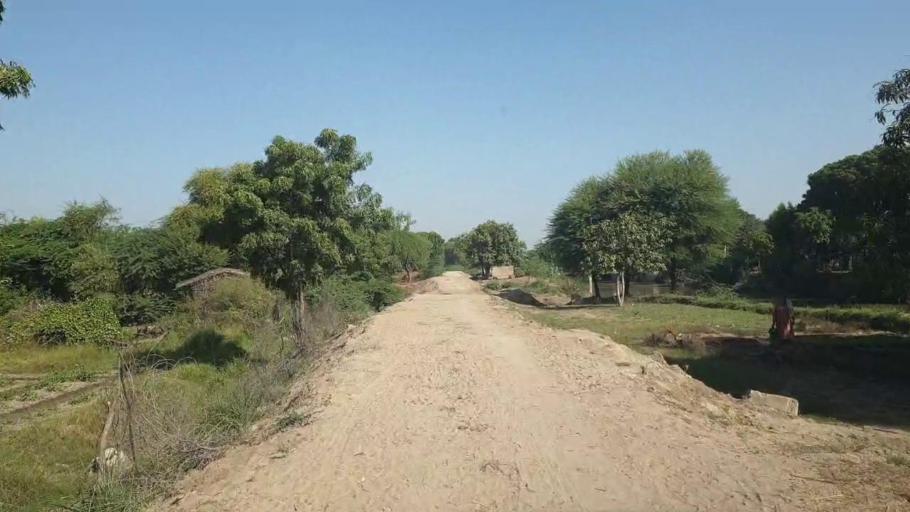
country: PK
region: Sindh
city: Talhar
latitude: 24.7751
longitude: 68.8054
